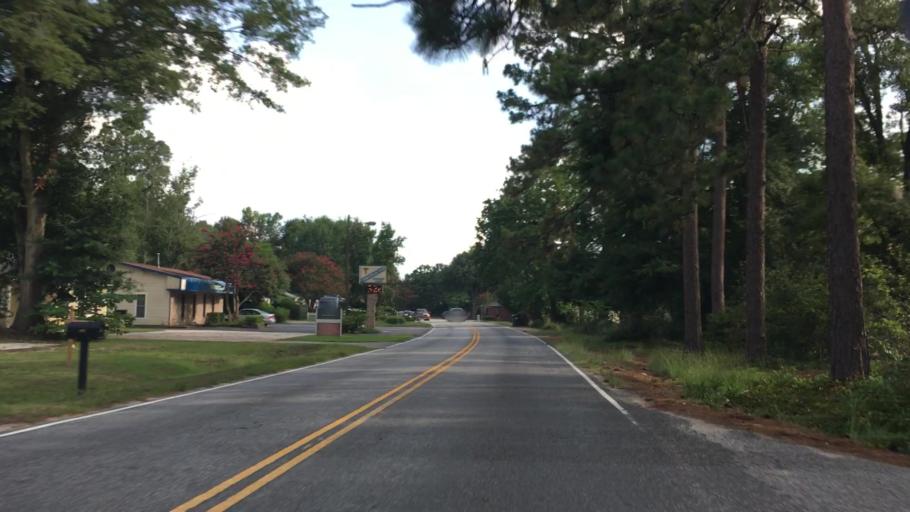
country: US
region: South Carolina
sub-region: Aiken County
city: Aiken
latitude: 33.5270
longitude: -81.7255
